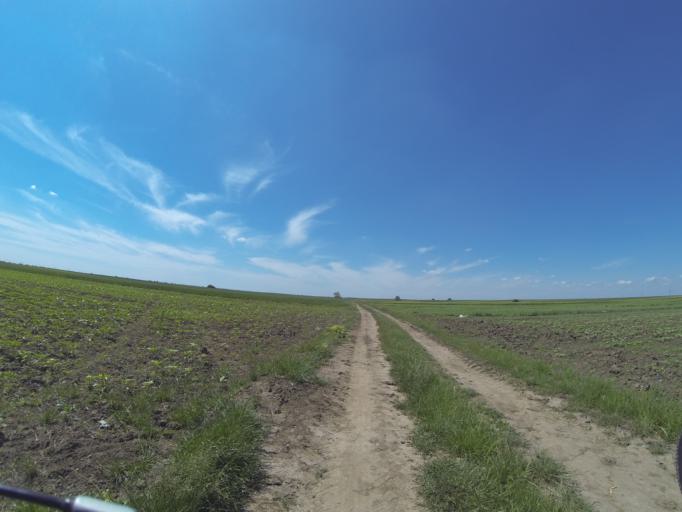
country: RO
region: Dolj
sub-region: Comuna Leu
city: Leu
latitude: 44.2133
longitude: 24.0272
